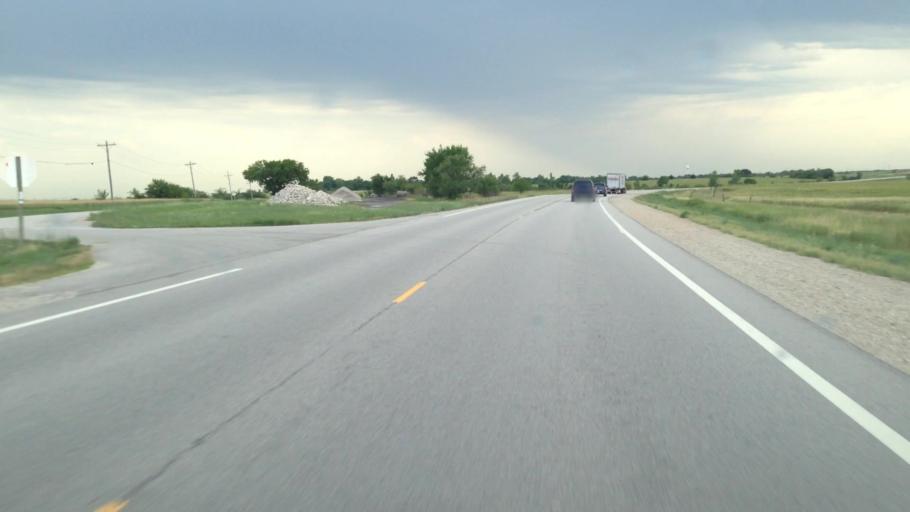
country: US
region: Kansas
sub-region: Coffey County
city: Burlington
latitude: 38.3001
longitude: -95.7289
